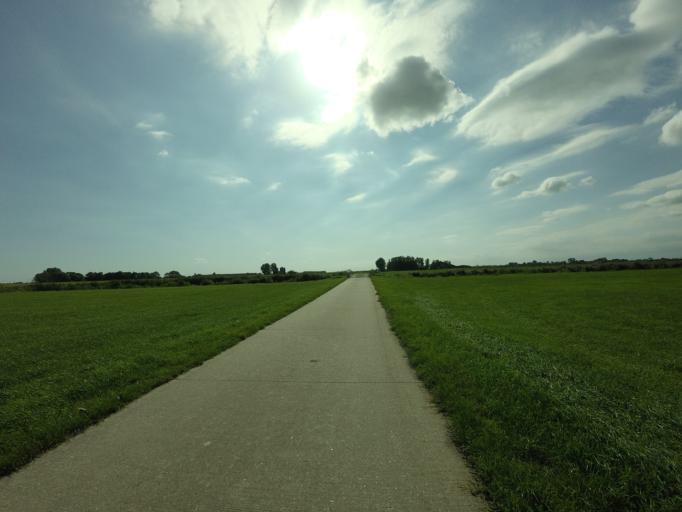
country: NL
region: Friesland
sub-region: Gemeente Littenseradiel
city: Makkum
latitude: 53.0884
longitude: 5.6348
